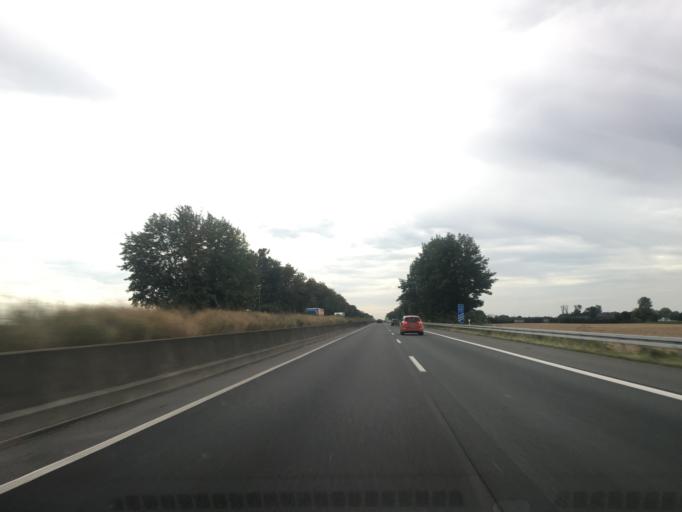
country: DE
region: North Rhine-Westphalia
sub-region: Regierungsbezirk Dusseldorf
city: Neubrueck
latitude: 51.1461
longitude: 6.6246
